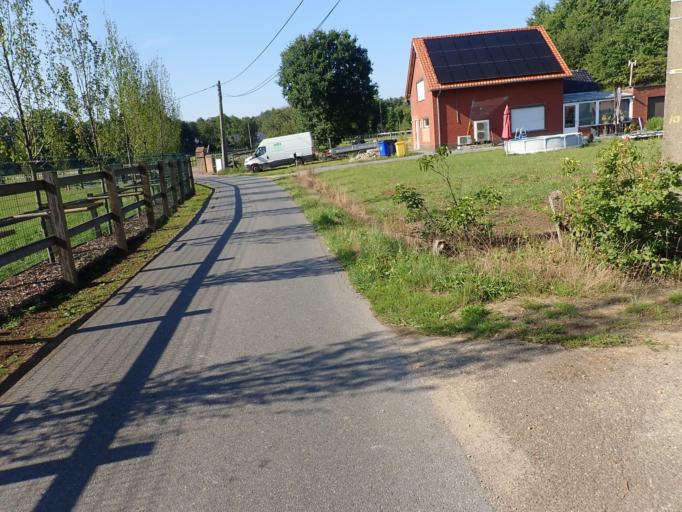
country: BE
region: Flanders
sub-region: Provincie Antwerpen
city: Herselt
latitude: 51.0497
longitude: 4.9138
